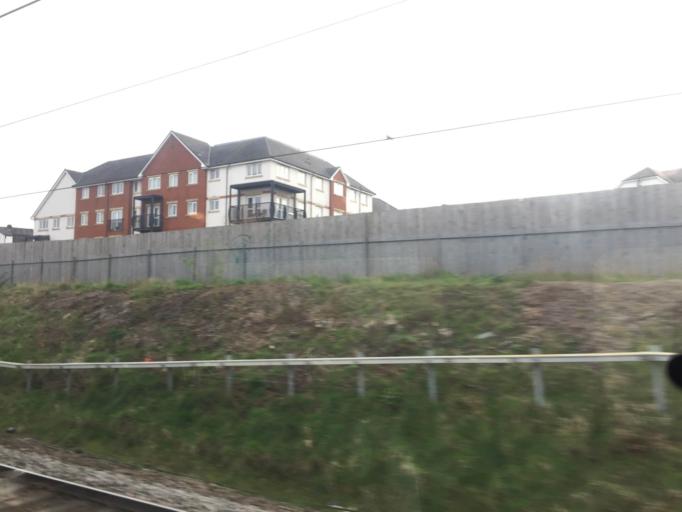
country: GB
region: England
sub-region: Warrington
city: Warrington
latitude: 53.3939
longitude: -2.6031
